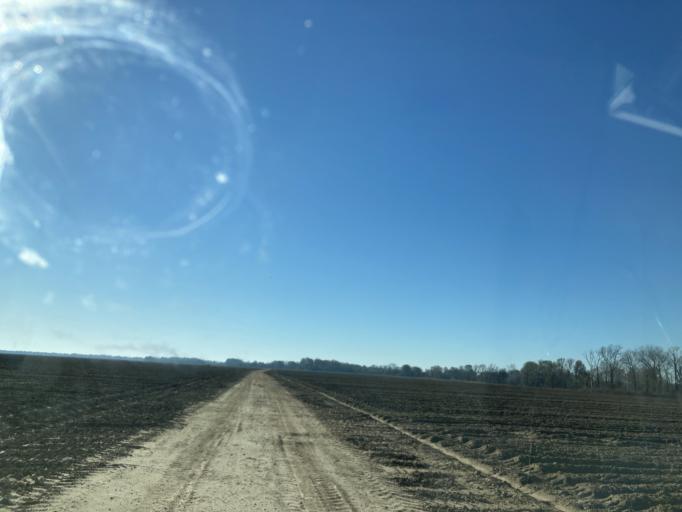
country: US
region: Mississippi
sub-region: Sharkey County
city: Rolling Fork
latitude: 32.8652
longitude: -90.6930
